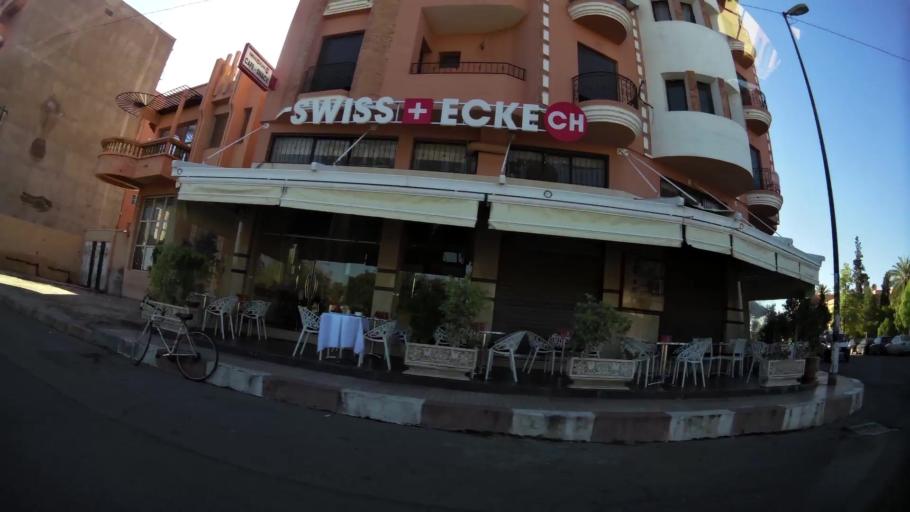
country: MA
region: Marrakech-Tensift-Al Haouz
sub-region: Marrakech
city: Marrakesh
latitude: 31.6481
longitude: -8.0142
